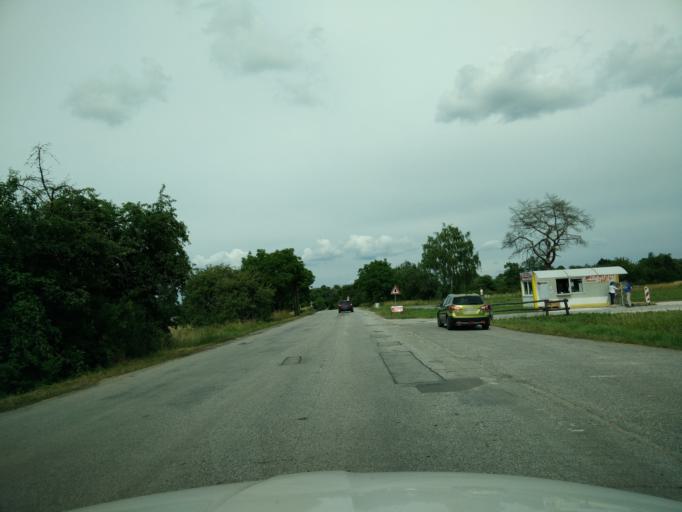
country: SK
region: Nitriansky
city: Novaky
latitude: 48.7316
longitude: 18.5639
